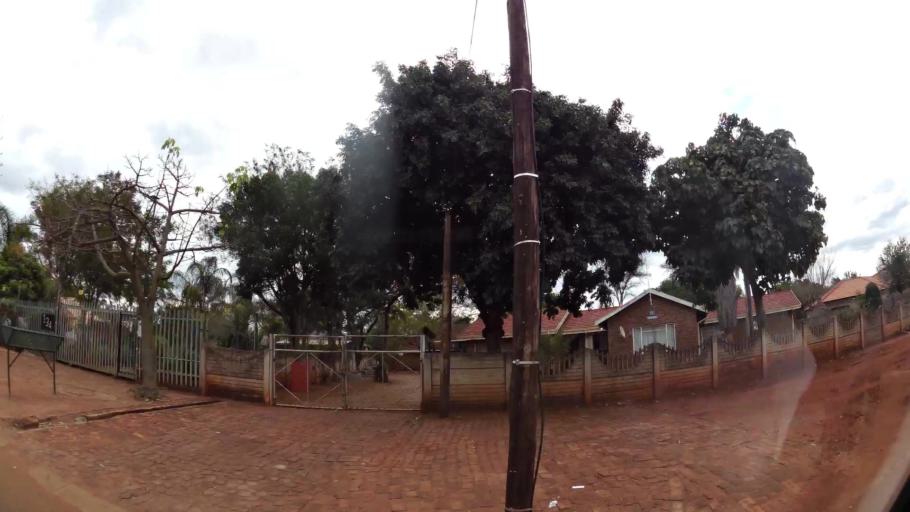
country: ZA
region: Limpopo
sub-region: Waterberg District Municipality
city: Modimolle
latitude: -24.5084
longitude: 28.7233
